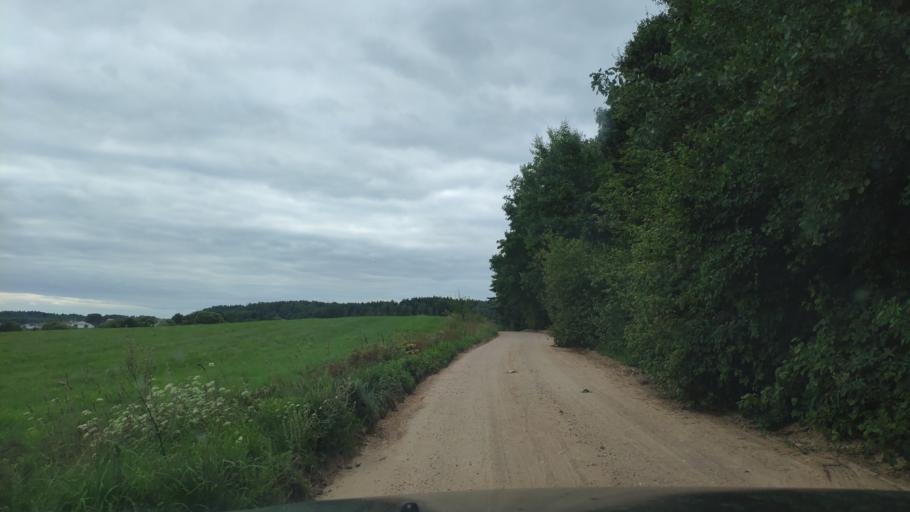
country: BY
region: Minsk
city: Khatsyezhyna
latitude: 53.9354
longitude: 27.2793
